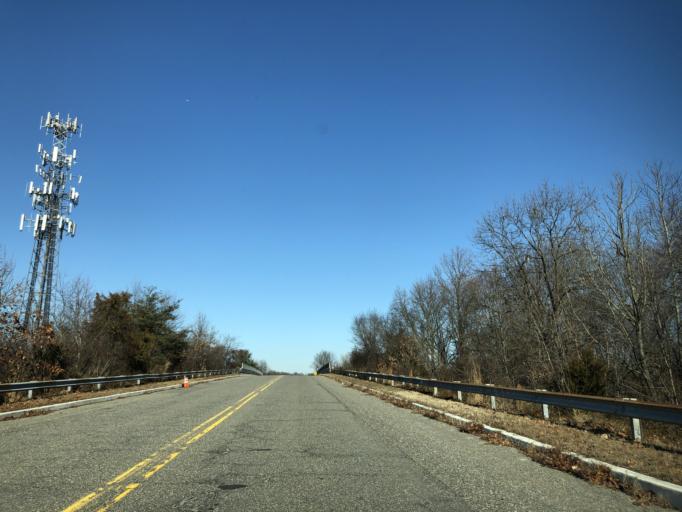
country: US
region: New Jersey
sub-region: Gloucester County
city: Beckett
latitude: 39.8015
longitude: -75.3413
